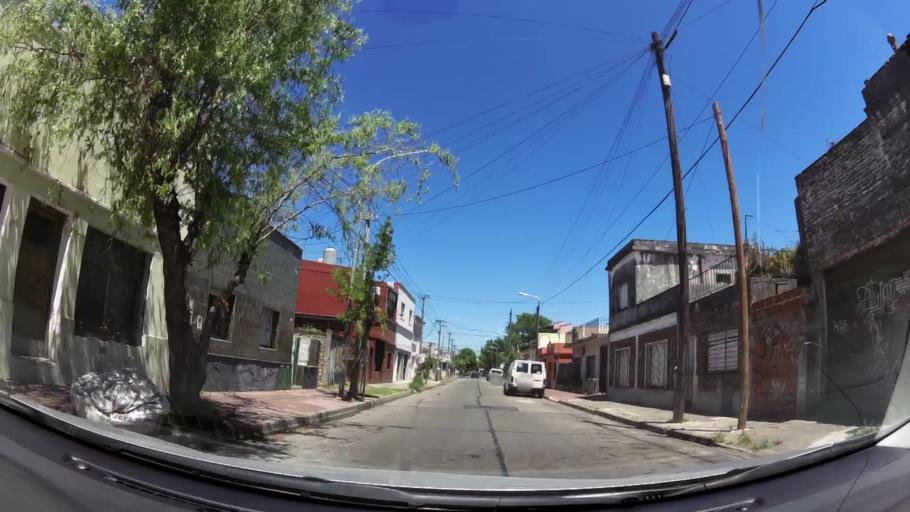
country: AR
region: Buenos Aires
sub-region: Partido de Tigre
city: Tigre
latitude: -34.4520
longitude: -58.5509
